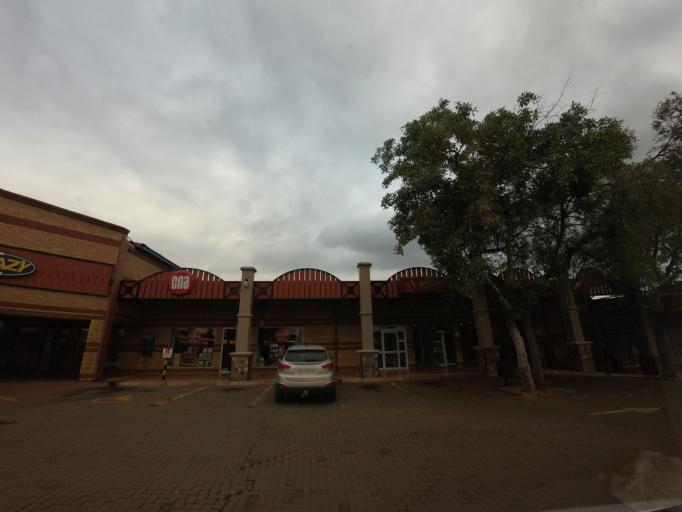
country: ZA
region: Mpumalanga
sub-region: Ehlanzeni District
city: Komatipoort
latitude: -25.4375
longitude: 31.9612
